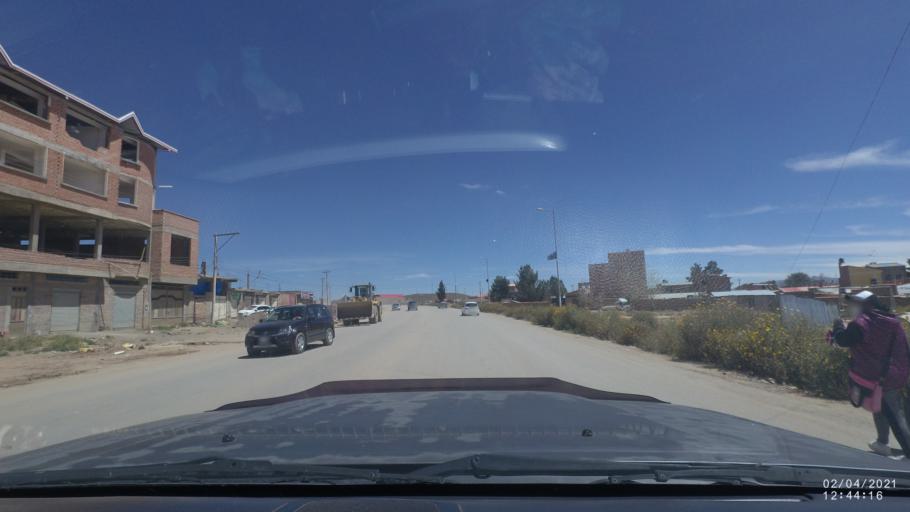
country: BO
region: Oruro
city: Oruro
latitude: -17.9280
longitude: -67.1271
